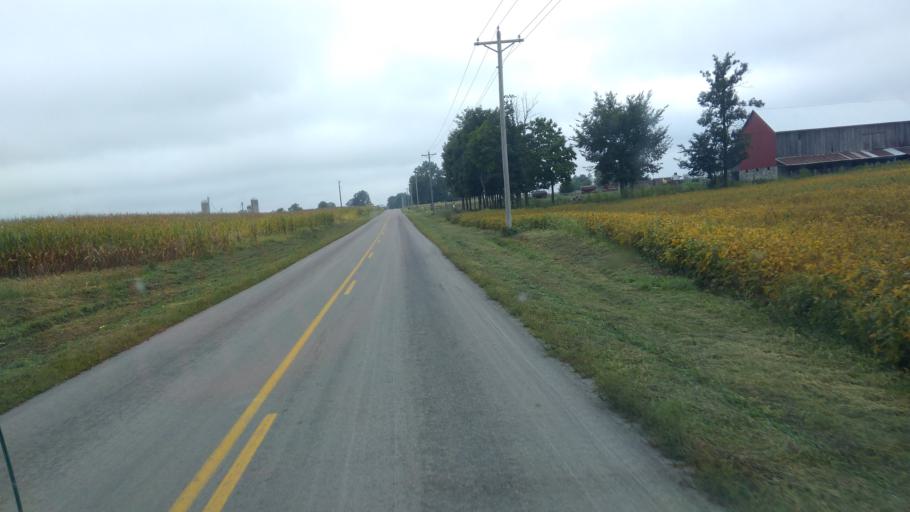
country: US
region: Ohio
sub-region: Hardin County
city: Kenton
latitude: 40.5730
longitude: -83.6448
